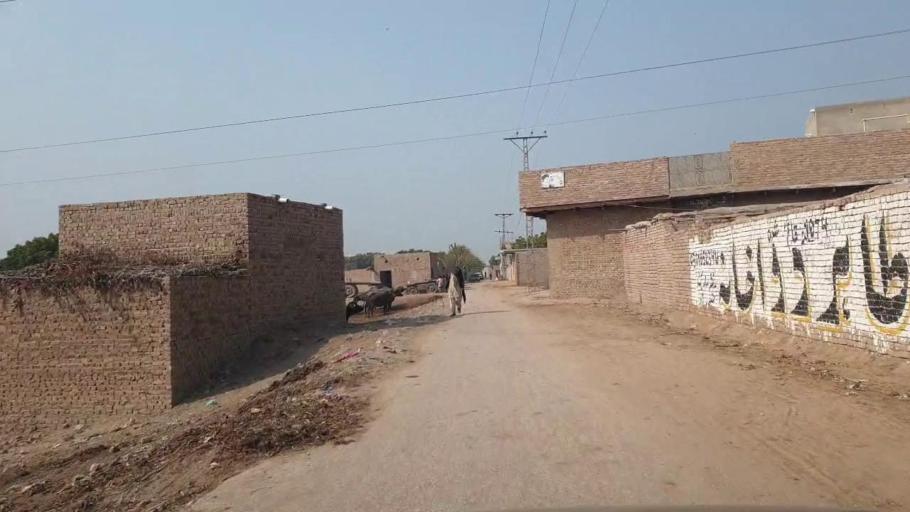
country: PK
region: Sindh
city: Hala
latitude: 25.8315
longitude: 68.4442
